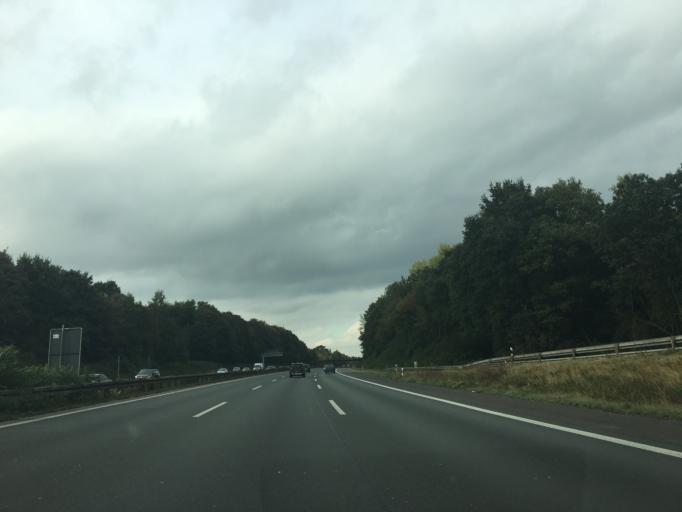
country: DE
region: North Rhine-Westphalia
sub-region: Regierungsbezirk Koln
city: Leverkusen
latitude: 51.0570
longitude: 6.9911
